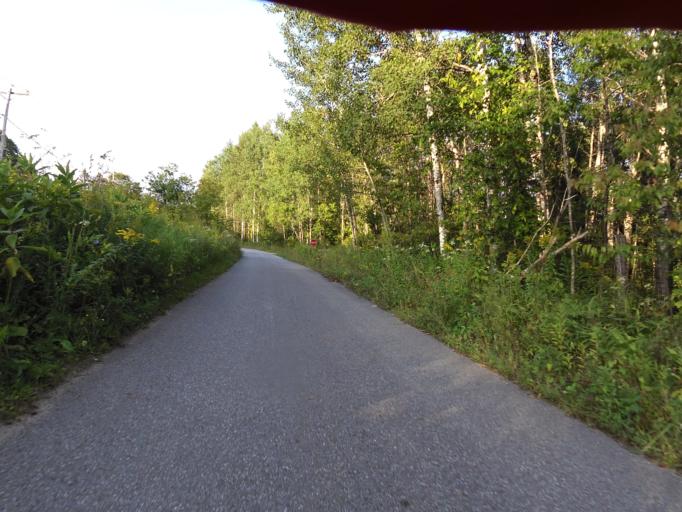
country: CA
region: Quebec
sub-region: Outaouais
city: Maniwaki
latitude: 46.3695
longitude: -75.9797
